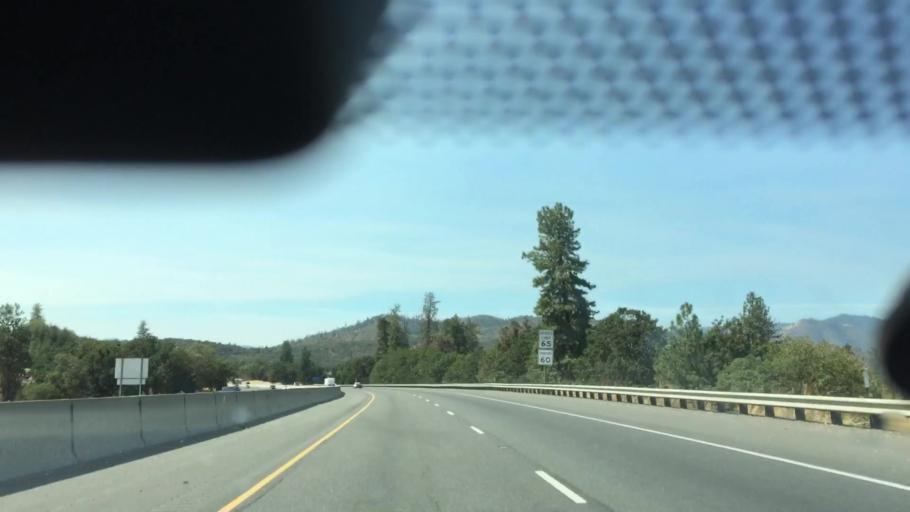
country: US
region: Oregon
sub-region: Jackson County
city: Central Point
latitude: 42.4095
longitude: -122.9556
